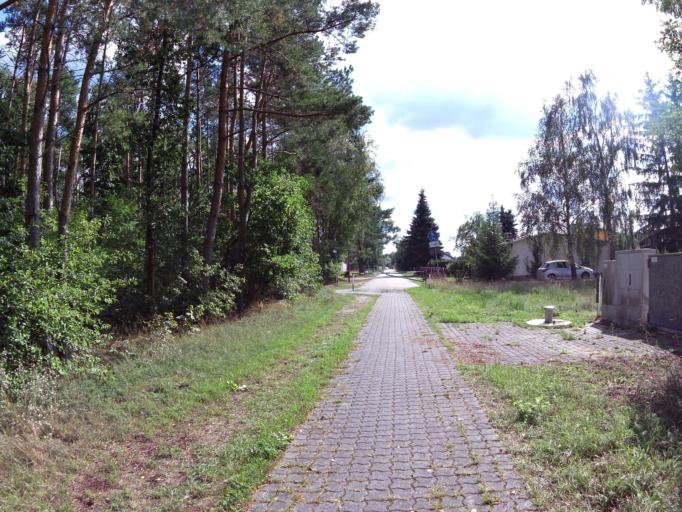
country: DE
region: Brandenburg
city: Storkow
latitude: 52.2202
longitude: 13.8730
